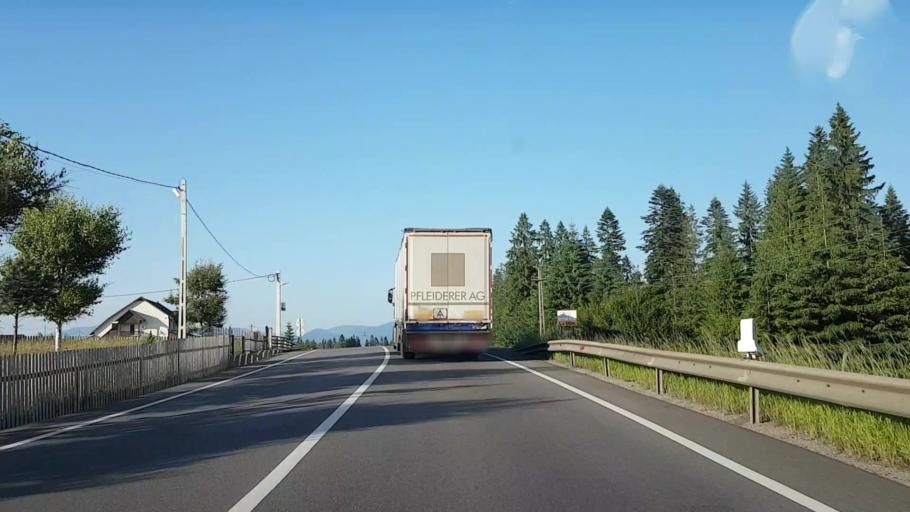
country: RO
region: Suceava
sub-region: Comuna Poiana Stampei
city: Poiana Stampei
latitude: 47.2927
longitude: 25.0799
